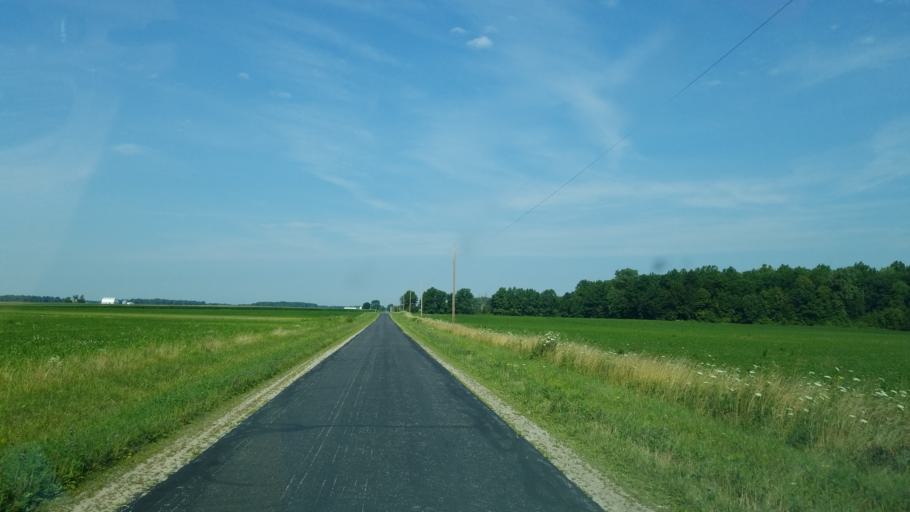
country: US
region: Ohio
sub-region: Huron County
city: Willard
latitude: 41.0374
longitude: -82.9235
